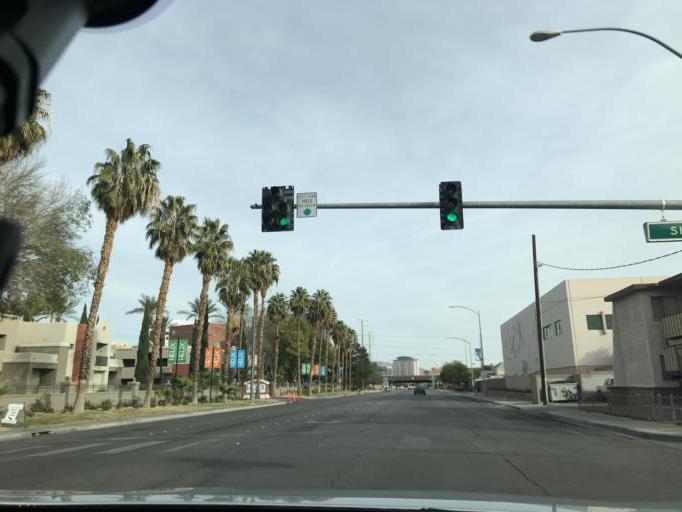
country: US
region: Nevada
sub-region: Clark County
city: Las Vegas
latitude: 36.1662
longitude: -115.1656
